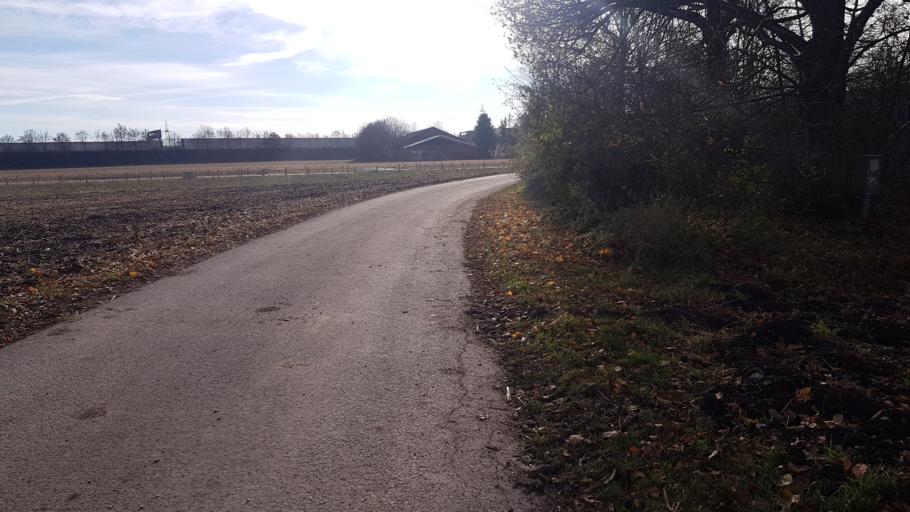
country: DE
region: Bavaria
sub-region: Upper Bavaria
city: Oberschleissheim
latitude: 48.2281
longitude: 11.5299
